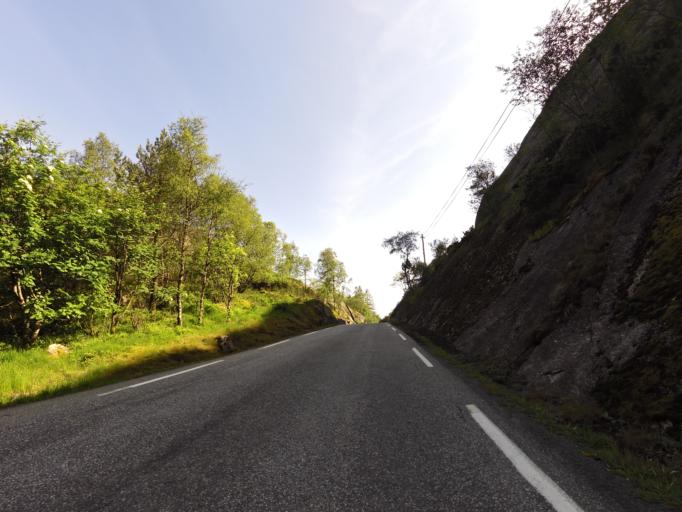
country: NO
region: Rogaland
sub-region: Sokndal
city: Hauge i Dalane
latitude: 58.3351
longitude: 6.3490
